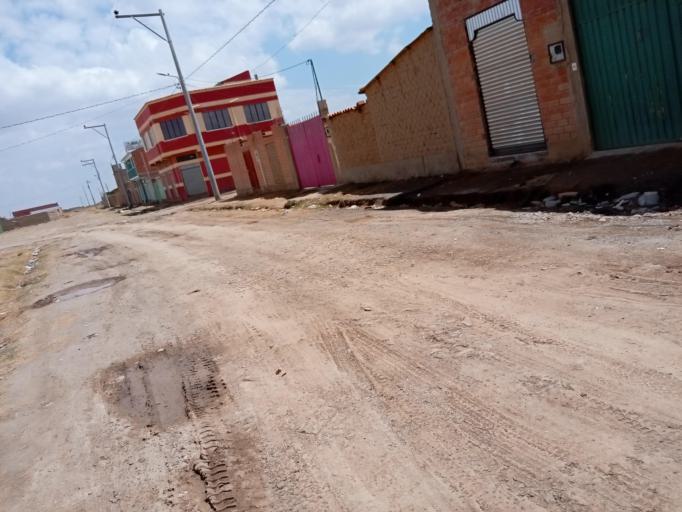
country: BO
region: La Paz
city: Batallas
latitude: -16.4077
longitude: -68.5420
